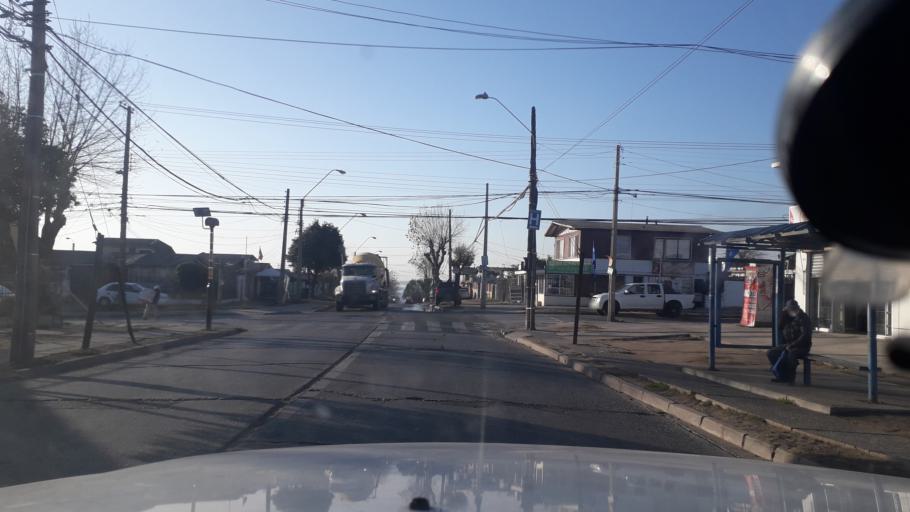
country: CL
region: Valparaiso
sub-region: Provincia de Valparaiso
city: Vina del Mar
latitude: -32.9261
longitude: -71.5166
